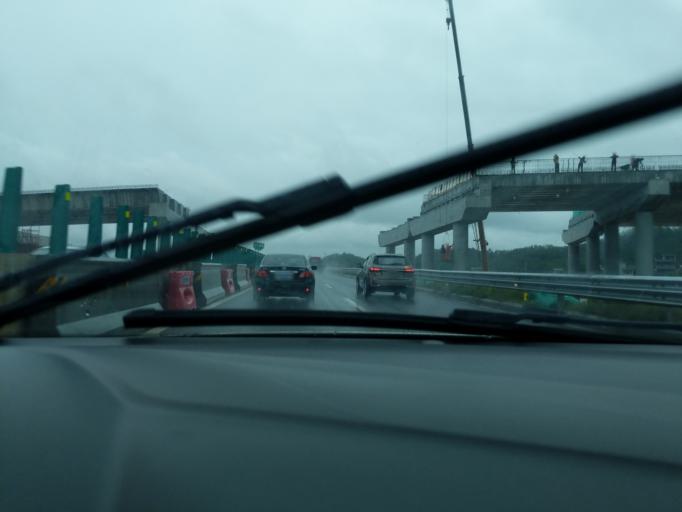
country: CN
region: Guangdong
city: Yueshan
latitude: 22.4631
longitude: 112.7151
